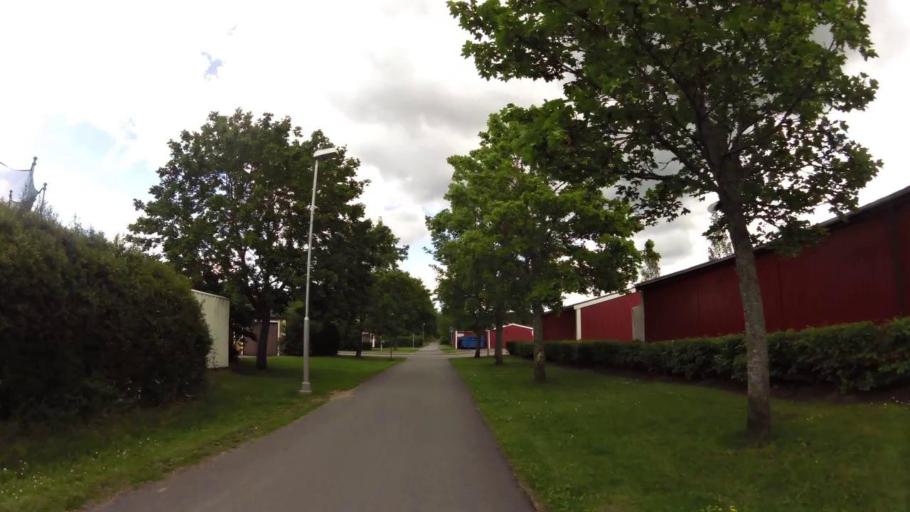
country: SE
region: OEstergoetland
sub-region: Linkopings Kommun
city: Ekangen
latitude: 58.4315
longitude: 15.6887
